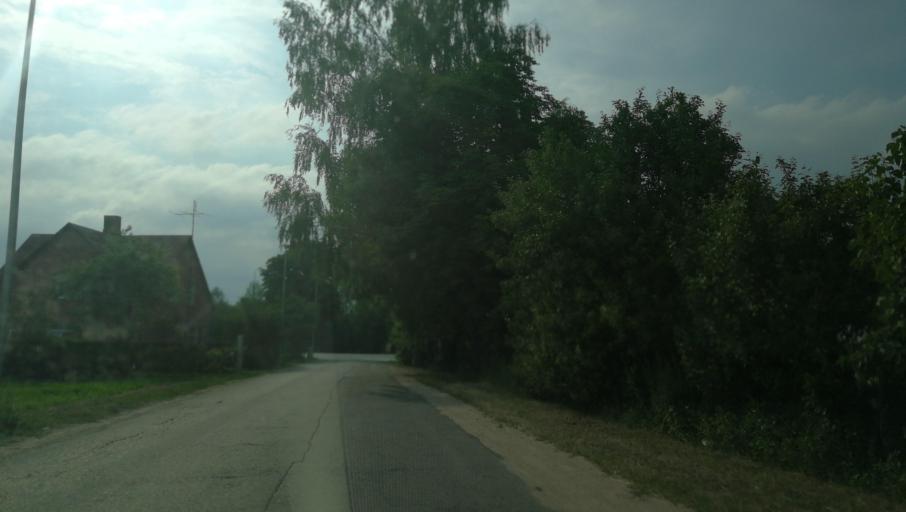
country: LV
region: Cesu Rajons
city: Cesis
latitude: 57.3210
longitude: 25.2937
